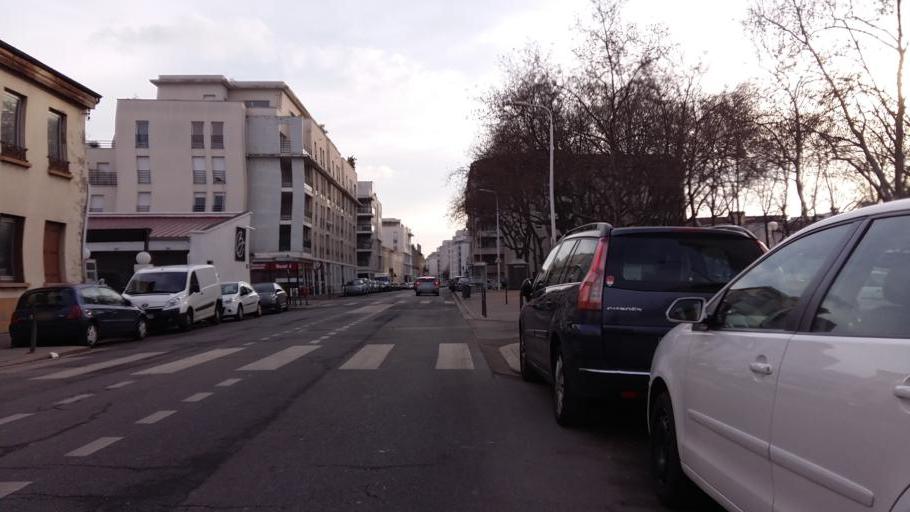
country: FR
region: Rhone-Alpes
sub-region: Departement du Rhone
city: Lyon
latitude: 45.7401
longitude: 4.8405
